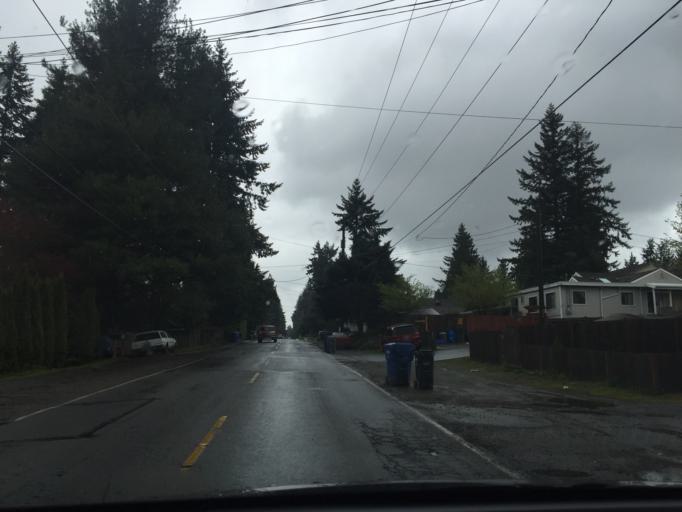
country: US
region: Washington
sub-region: King County
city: Lake Forest Park
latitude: 47.7249
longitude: -122.2964
